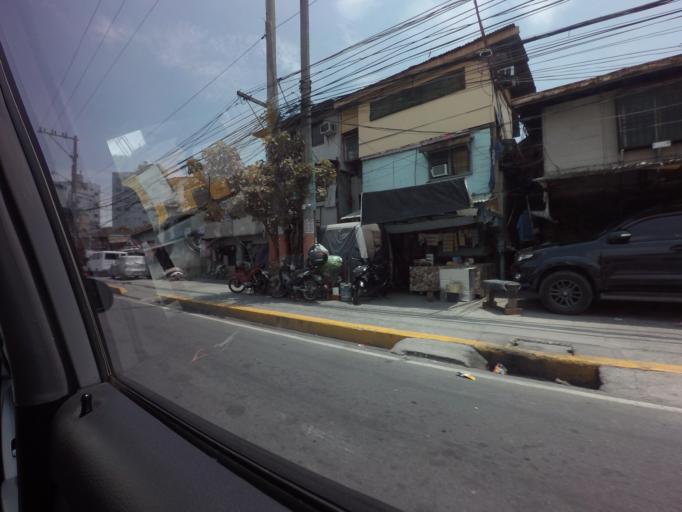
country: PH
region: Metro Manila
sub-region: City of Manila
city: Quiapo
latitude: 14.5890
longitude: 121.0017
